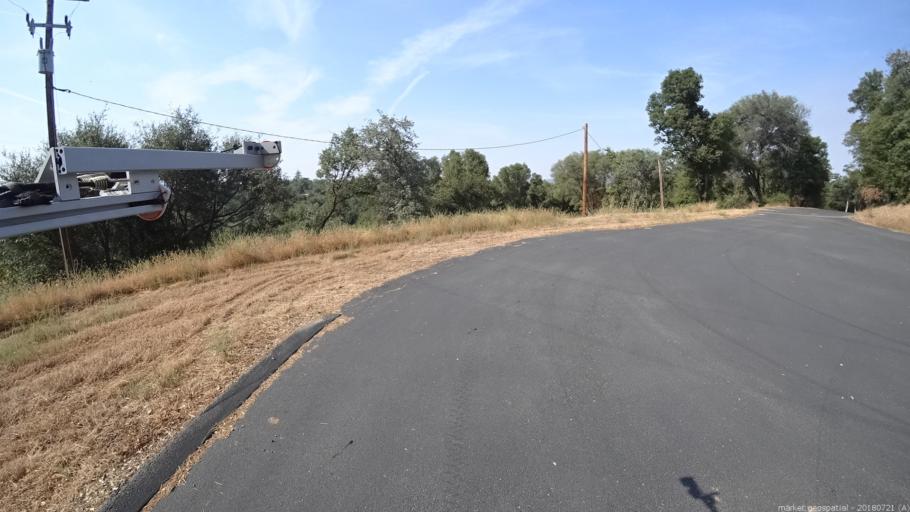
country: US
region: California
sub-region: Fresno County
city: Auberry
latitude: 37.2299
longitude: -119.5214
